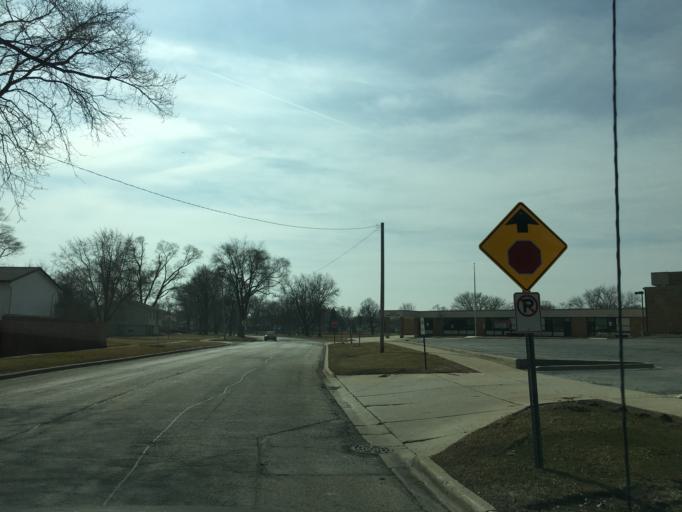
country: US
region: Illinois
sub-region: Cook County
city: Schaumburg
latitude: 42.0395
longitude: -88.0931
